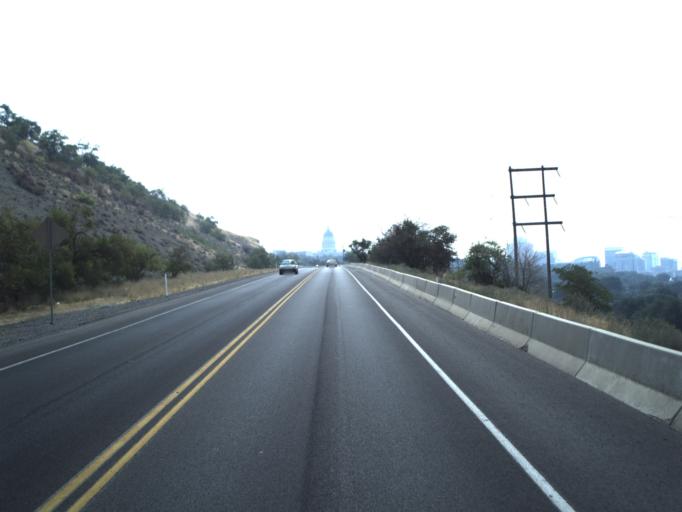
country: US
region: Utah
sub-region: Salt Lake County
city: Salt Lake City
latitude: 40.7900
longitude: -111.8990
